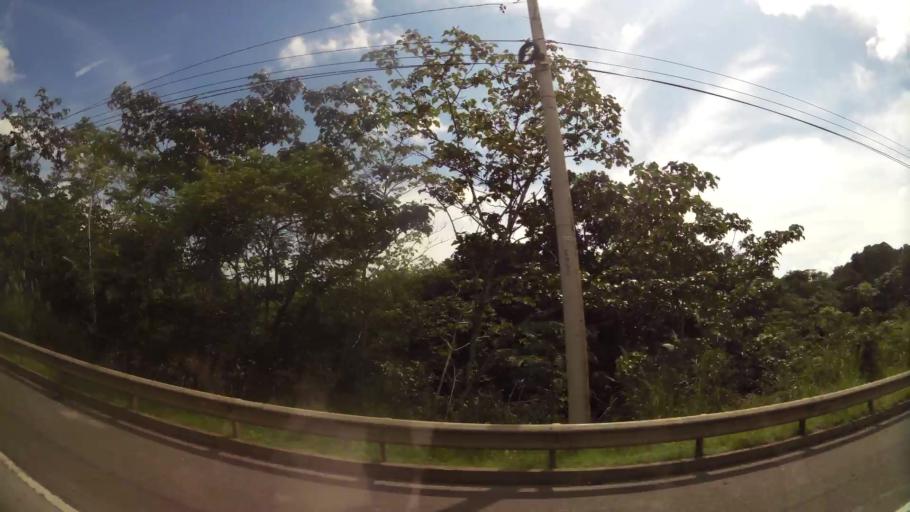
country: PA
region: Panama
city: Las Cumbres
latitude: 9.0407
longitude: -79.5583
